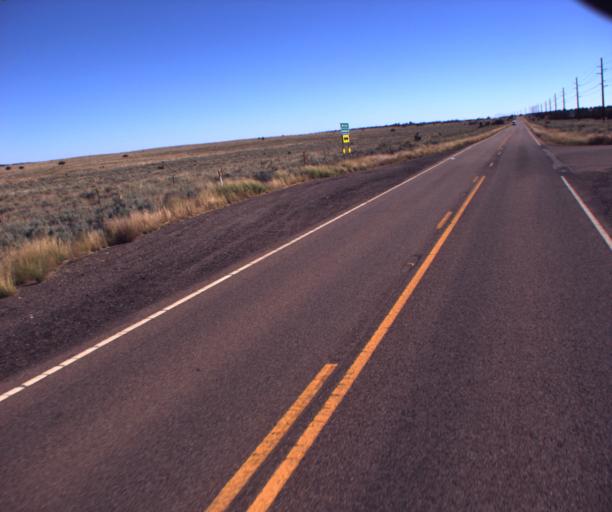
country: US
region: Arizona
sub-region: Navajo County
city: Taylor
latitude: 34.4831
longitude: -110.2800
